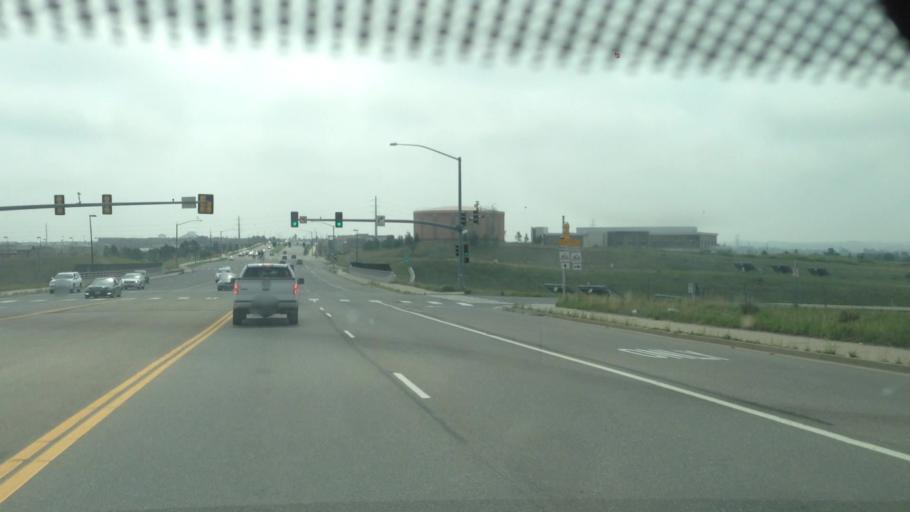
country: US
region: Colorado
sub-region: Douglas County
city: Parker
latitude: 39.6018
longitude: -104.7158
